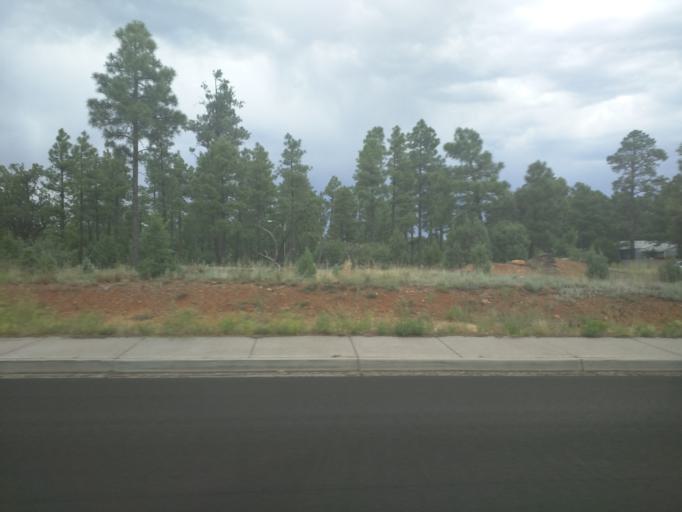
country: US
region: Arizona
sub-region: Navajo County
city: Show Low
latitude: 34.2422
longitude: -110.0429
